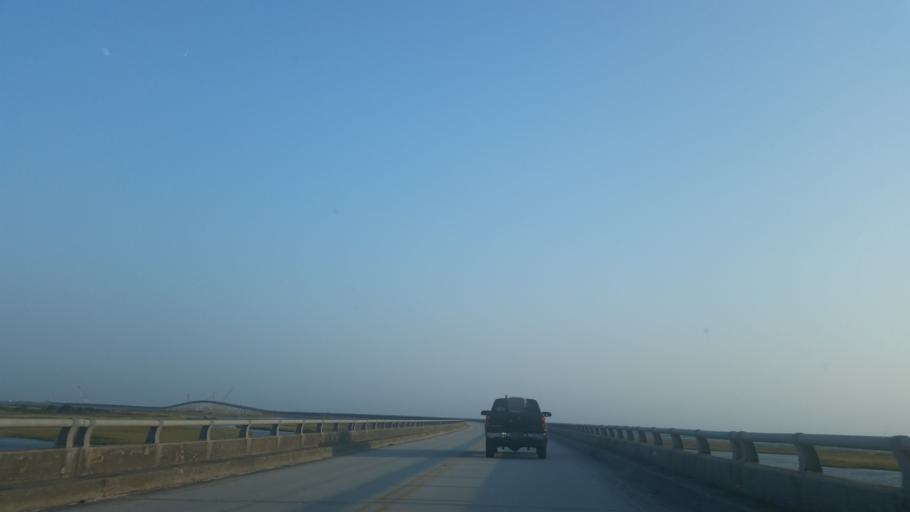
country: US
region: North Carolina
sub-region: Dare County
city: Wanchese
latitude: 35.7850
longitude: -75.5468
